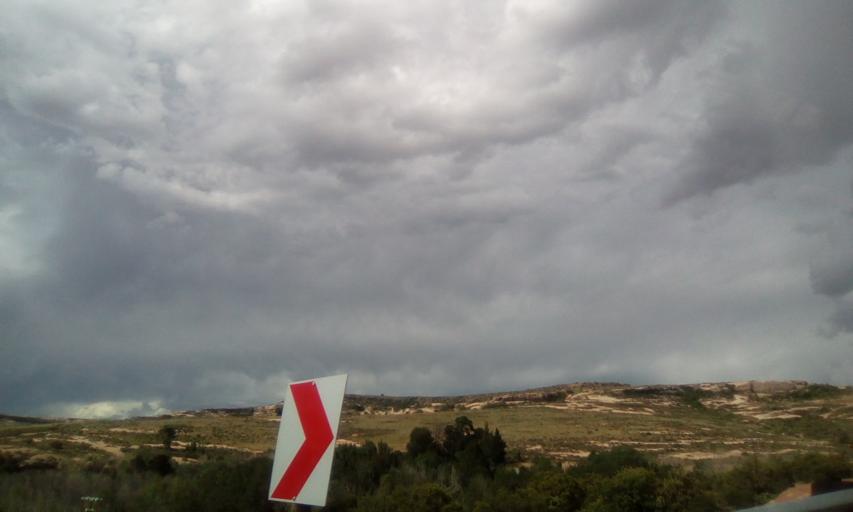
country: ZA
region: Orange Free State
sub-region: Thabo Mofutsanyana District Municipality
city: Ladybrand
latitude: -29.2493
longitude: 27.4360
